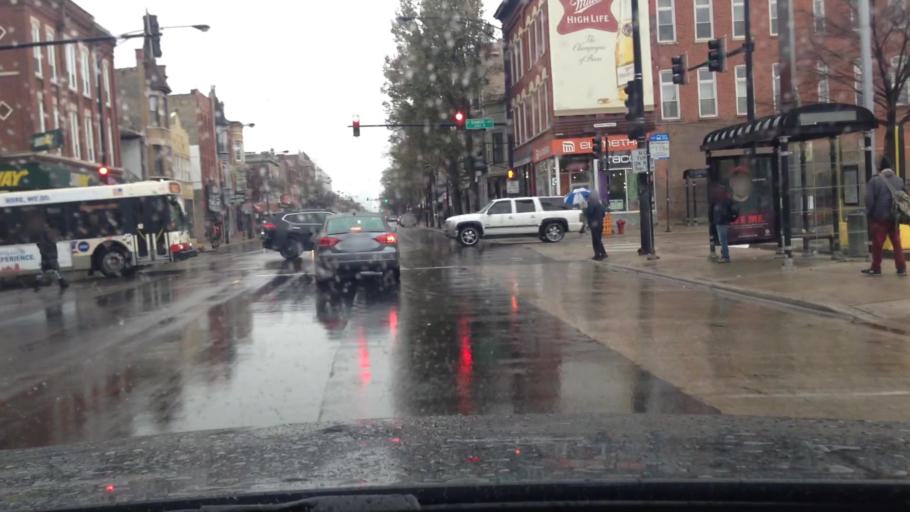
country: US
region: Illinois
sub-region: Cook County
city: Chicago
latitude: 41.8959
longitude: -87.6775
